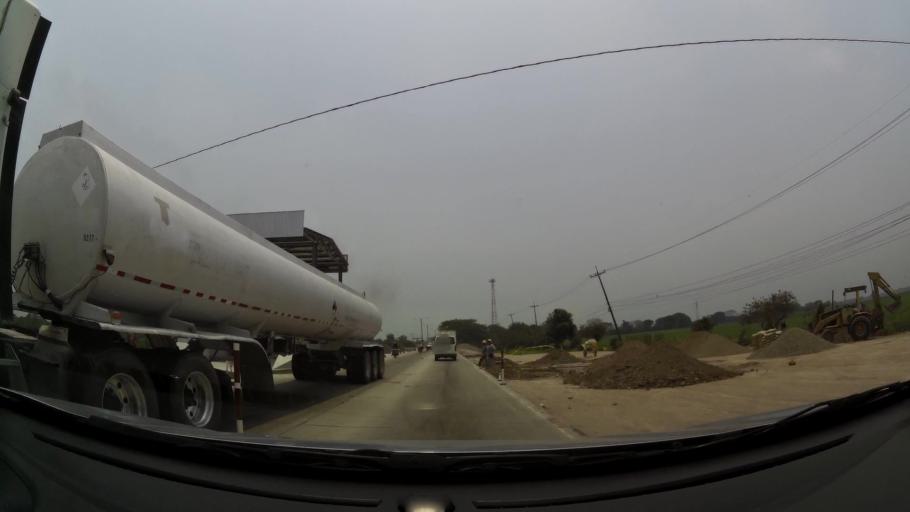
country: HN
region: Yoro
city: El Progreso
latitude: 15.4118
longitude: -87.8544
